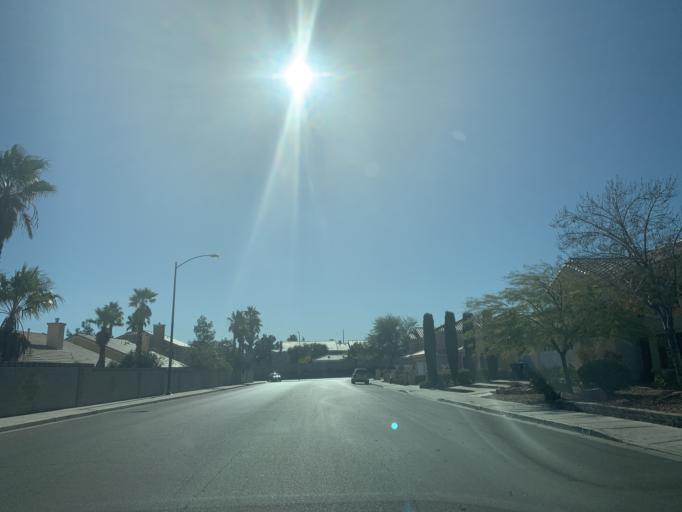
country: US
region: Nevada
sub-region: Clark County
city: Summerlin South
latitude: 36.1178
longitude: -115.2925
